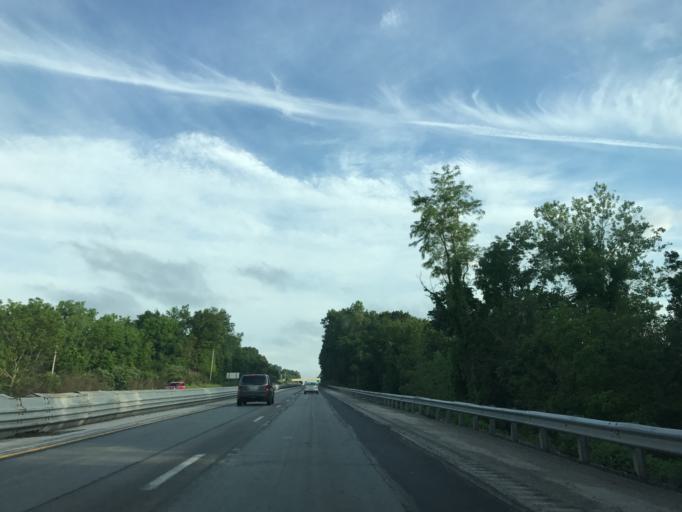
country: US
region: Pennsylvania
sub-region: York County
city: Loganville
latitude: 39.8519
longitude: -76.6902
